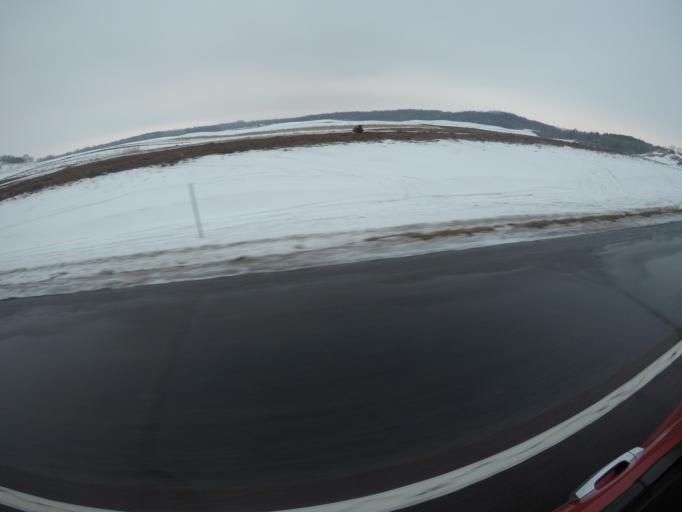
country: US
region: Minnesota
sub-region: Dakota County
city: Rosemount
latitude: 44.6859
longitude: -93.0197
